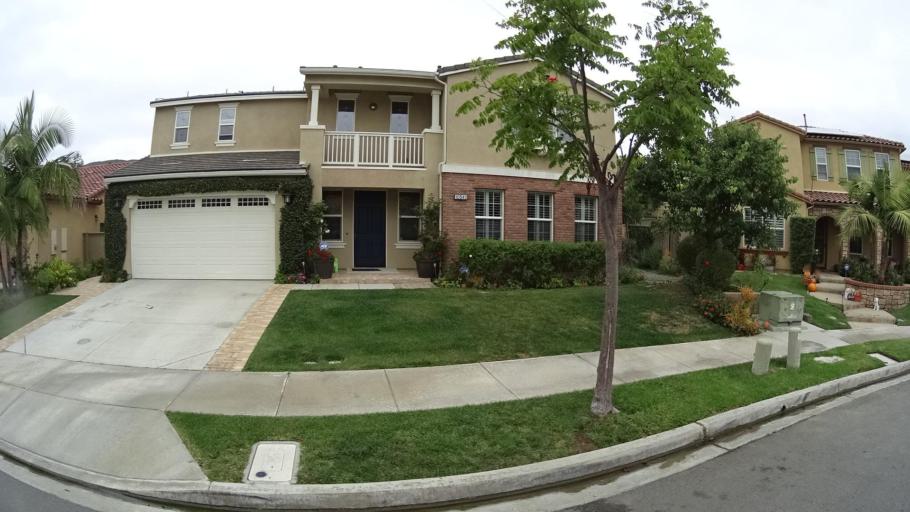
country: US
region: California
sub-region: San Diego County
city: Escondido
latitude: 33.0392
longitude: -117.1132
